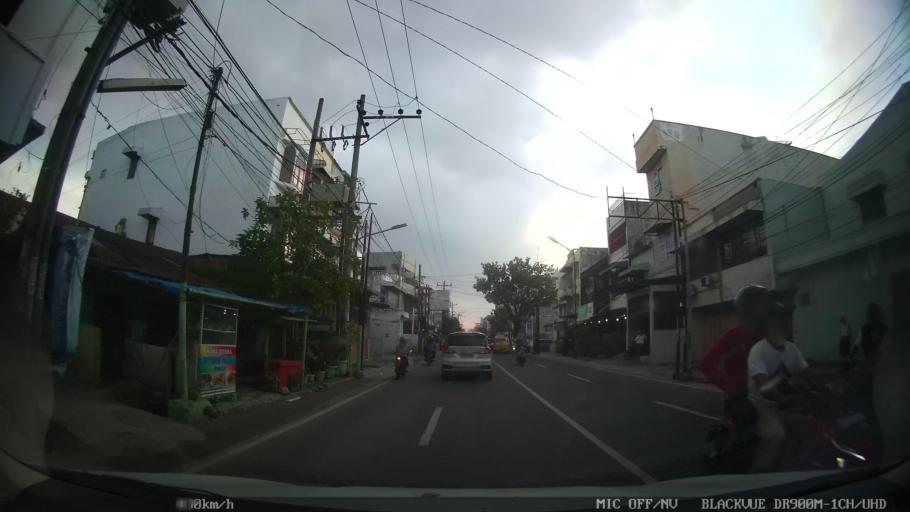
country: ID
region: North Sumatra
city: Medan
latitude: 3.5821
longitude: 98.6985
